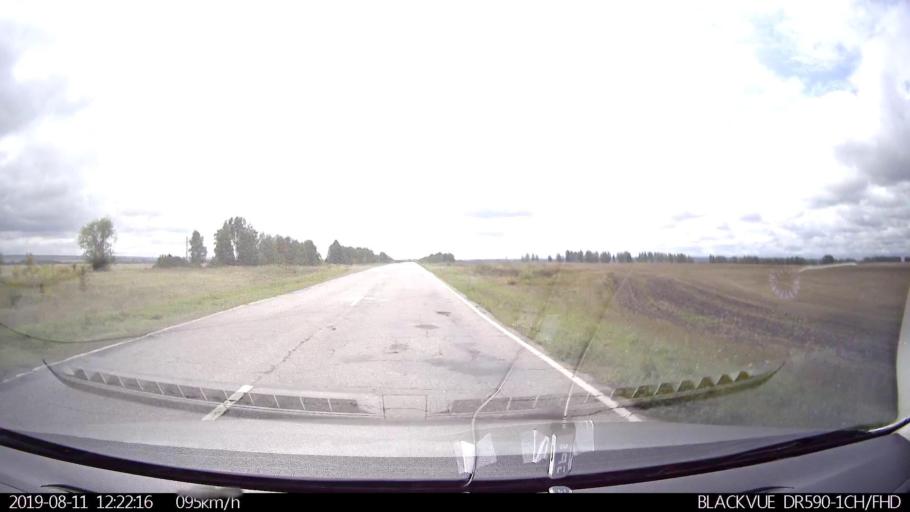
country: RU
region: Ulyanovsk
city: Ignatovka
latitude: 53.9102
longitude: 47.9547
